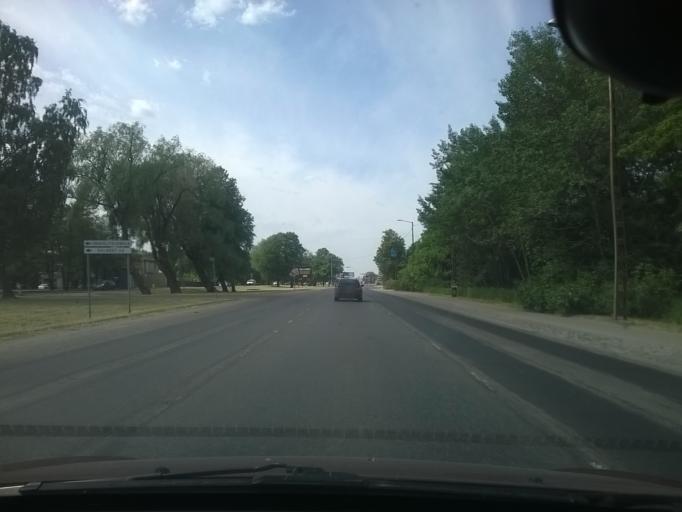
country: EE
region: Harju
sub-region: Tallinna linn
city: Tallinn
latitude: 59.4285
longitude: 24.6769
